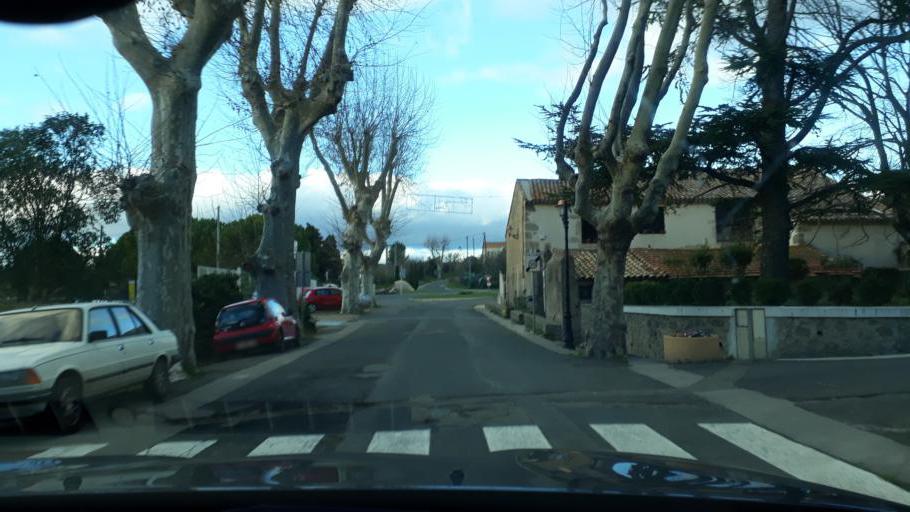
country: FR
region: Languedoc-Roussillon
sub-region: Departement de l'Herault
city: Nissan-lez-Enserune
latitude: 43.2925
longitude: 3.1276
